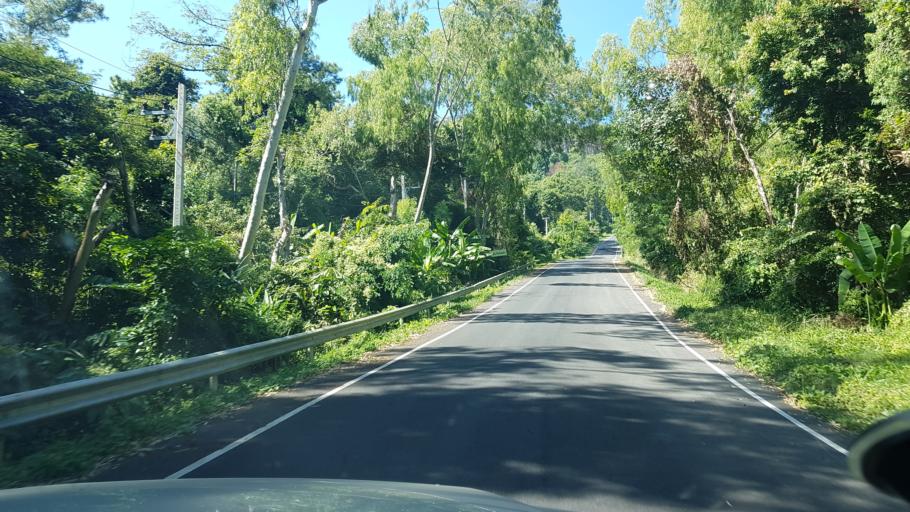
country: TH
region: Phetchabun
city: Khao Kho
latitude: 16.5527
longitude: 100.9816
